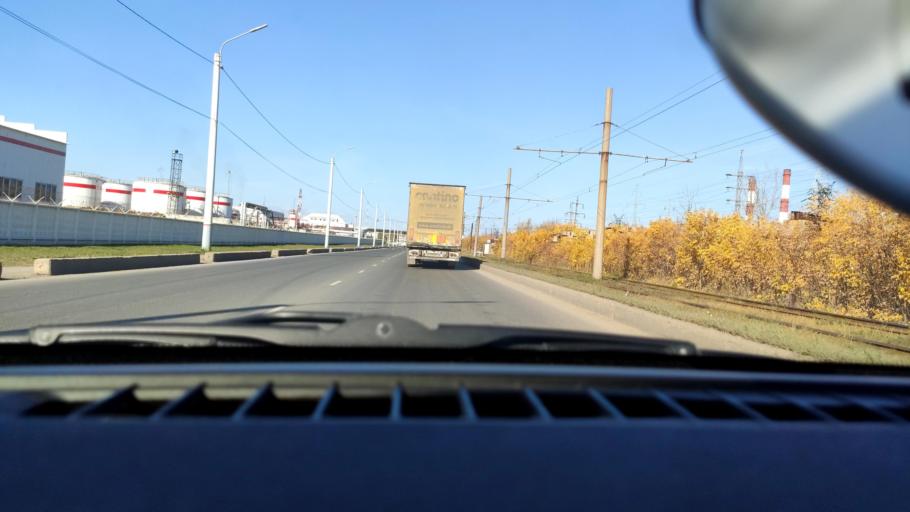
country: RU
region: Perm
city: Gamovo
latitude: 57.9180
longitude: 56.1498
